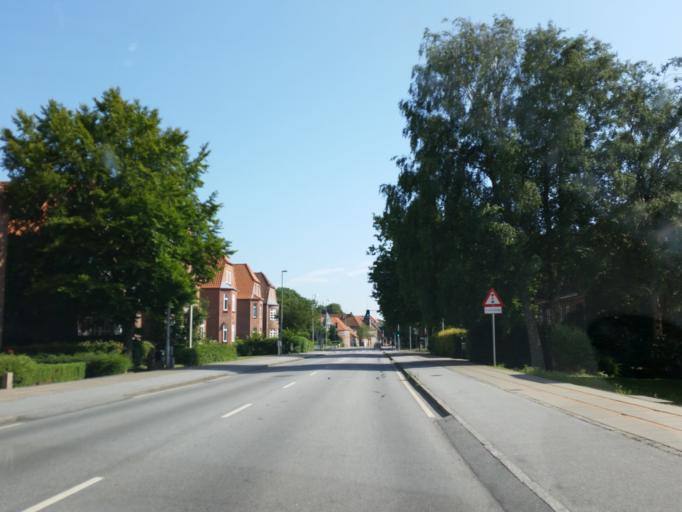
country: DK
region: South Denmark
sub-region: Tonder Kommune
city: Tonder
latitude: 54.9410
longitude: 8.8734
